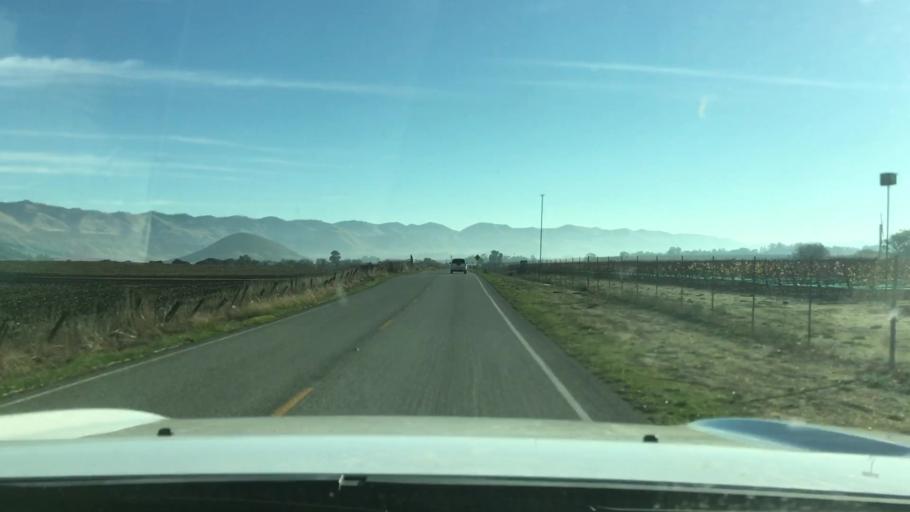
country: US
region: California
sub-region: San Luis Obispo County
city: San Luis Obispo
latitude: 35.2358
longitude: -120.6705
